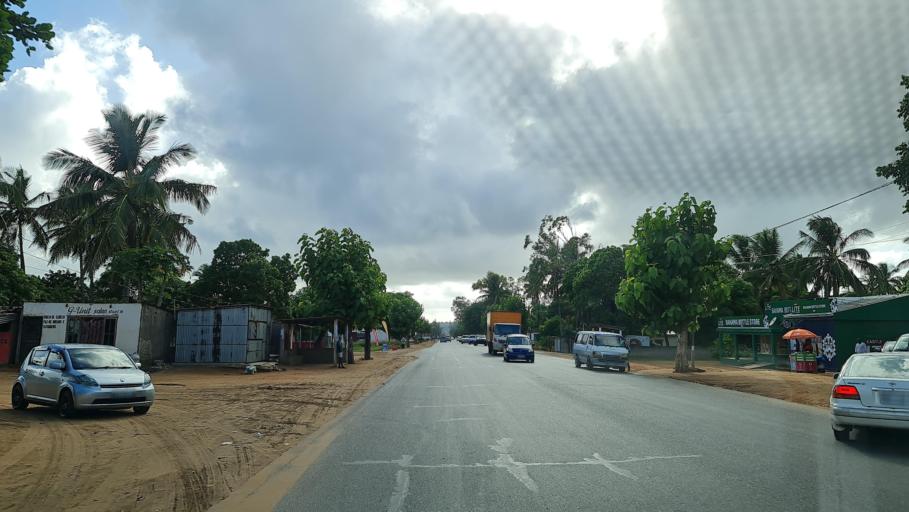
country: MZ
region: Gaza
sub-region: Xai-Xai District
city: Xai-Xai
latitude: -25.0557
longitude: 33.6904
